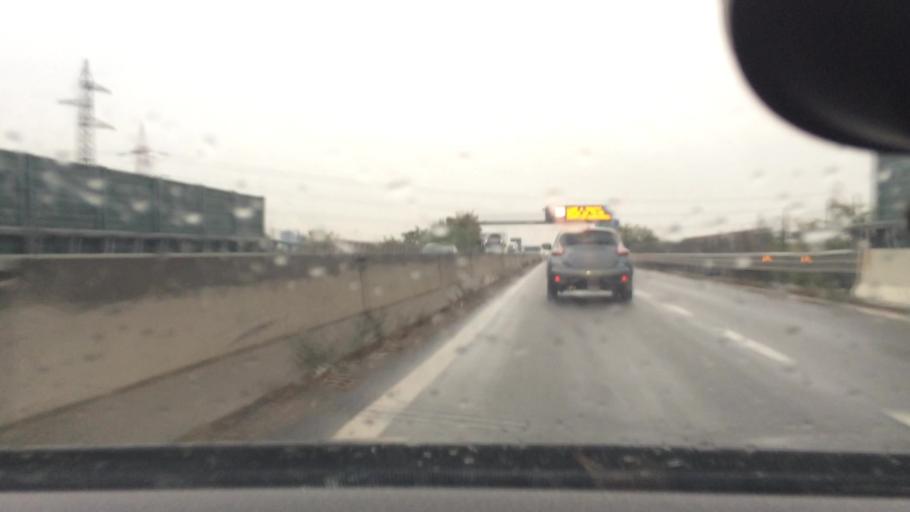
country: IT
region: Lombardy
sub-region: Citta metropolitana di Milano
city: Rho
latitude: 45.5283
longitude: 9.0562
